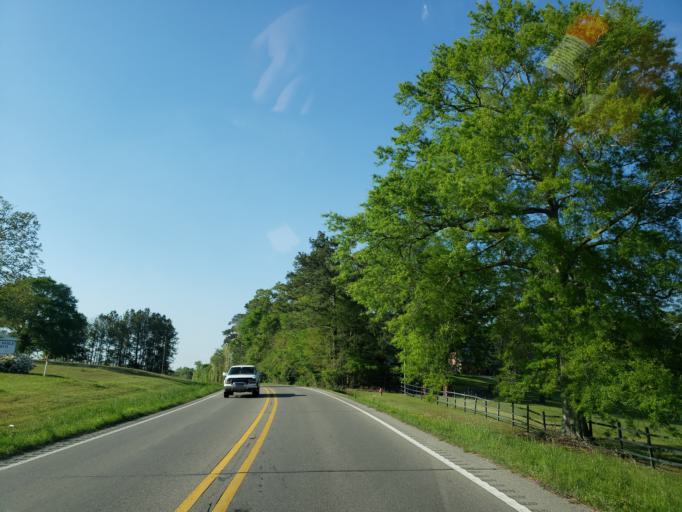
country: US
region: Mississippi
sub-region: Jones County
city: Laurel
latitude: 31.6747
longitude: -89.1090
